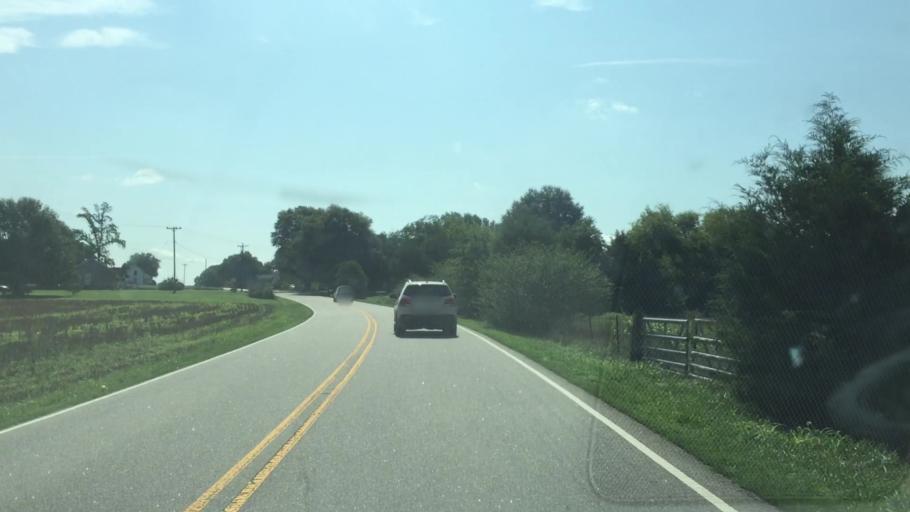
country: US
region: North Carolina
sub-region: Anson County
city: Burnsville
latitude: 35.1048
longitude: -80.3255
